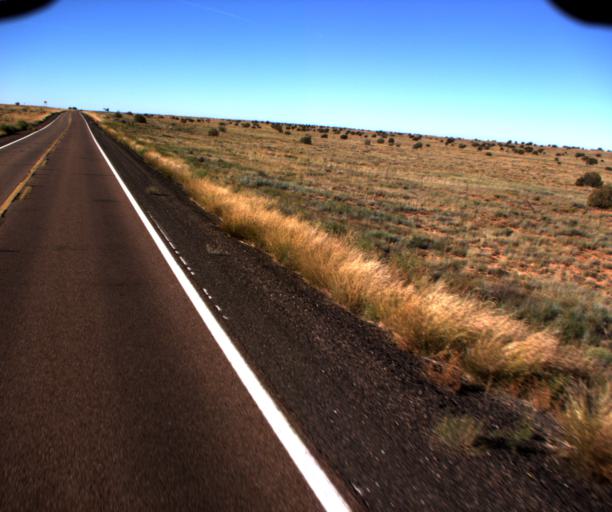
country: US
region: Arizona
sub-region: Navajo County
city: Holbrook
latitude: 34.7605
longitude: -110.2490
